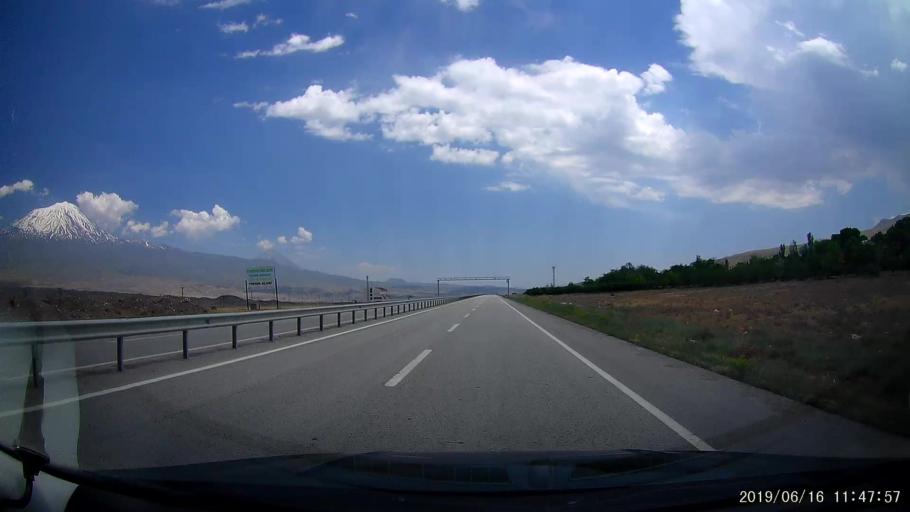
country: TR
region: Agri
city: Dogubayazit
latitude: 39.5582
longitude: 44.1360
